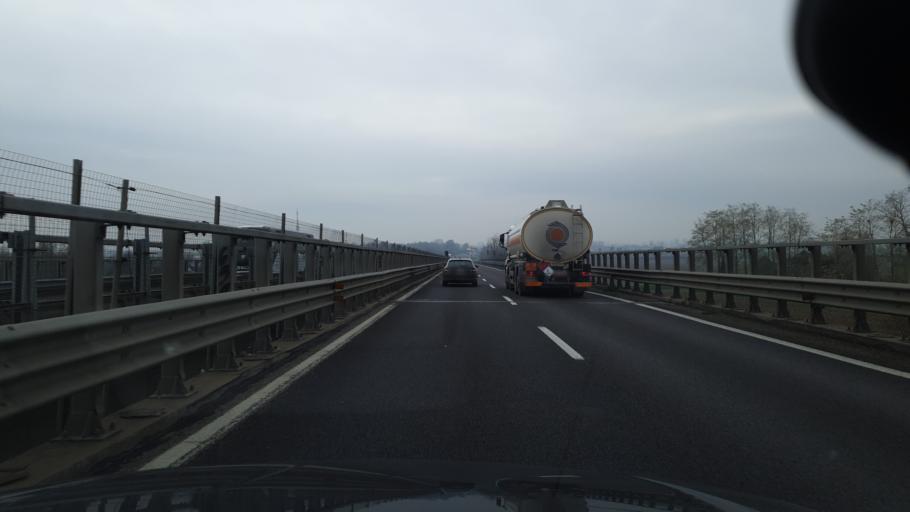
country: IT
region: Veneto
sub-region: Provincia di Padova
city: Boara Pisani
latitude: 45.0934
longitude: 11.7495
